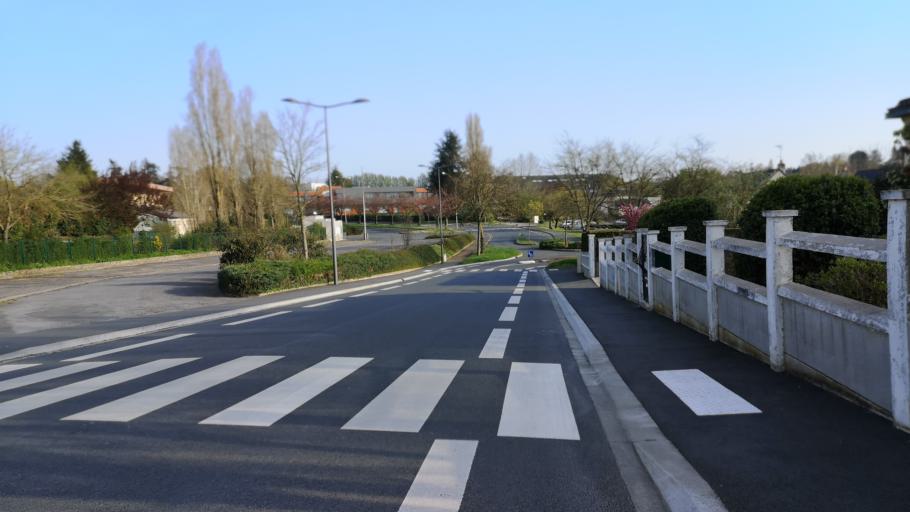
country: FR
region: Pays de la Loire
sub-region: Departement de Maine-et-Loire
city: Chemille-Melay
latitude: 47.2154
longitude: -0.7266
